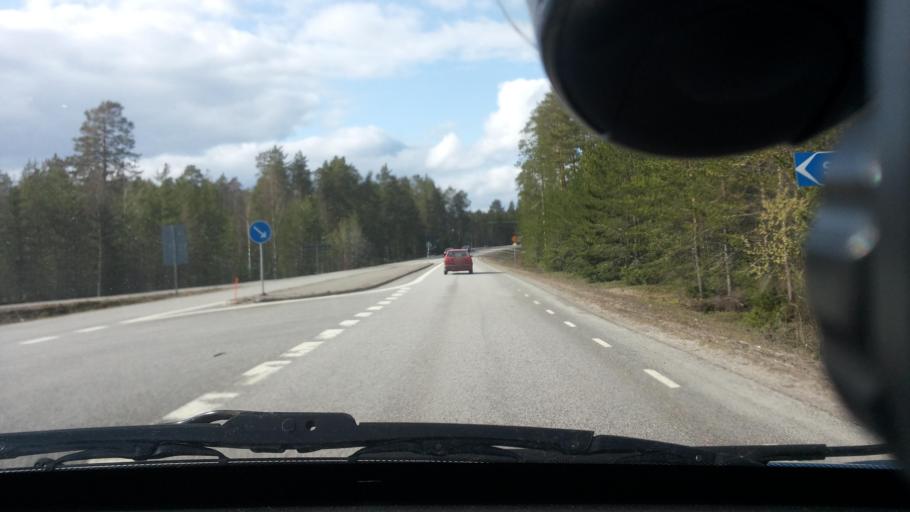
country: SE
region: Norrbotten
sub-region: Lulea Kommun
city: Gammelstad
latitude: 65.5984
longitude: 22.0433
